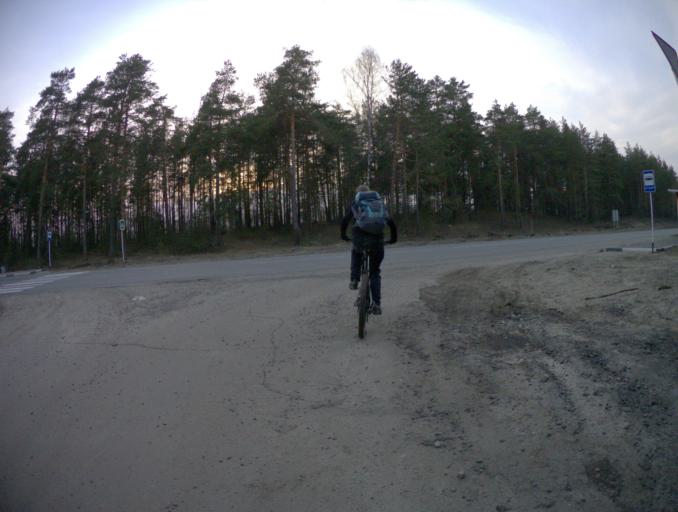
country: RU
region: Vladimir
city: Kommunar
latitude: 56.0682
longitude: 40.4329
